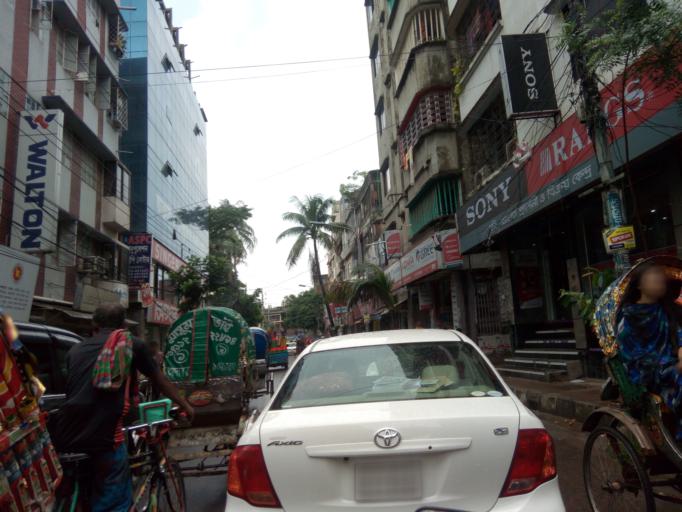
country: BD
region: Dhaka
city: Azimpur
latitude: 23.7615
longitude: 90.3614
